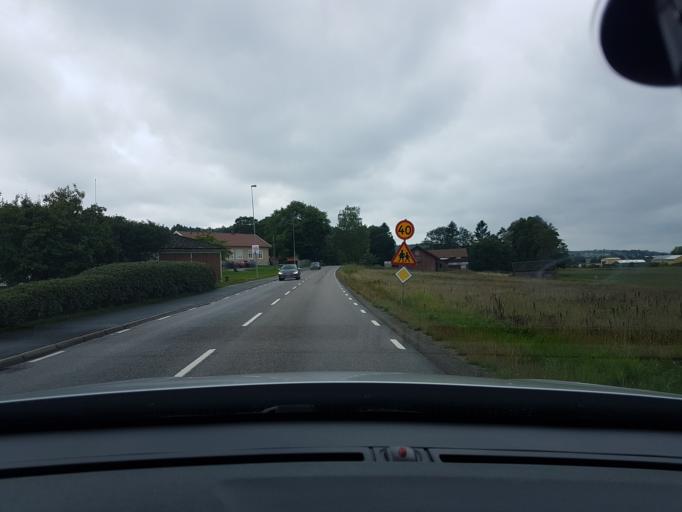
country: SE
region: Vaestra Goetaland
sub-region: Ale Kommun
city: Skepplanda
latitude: 57.9826
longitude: 12.2035
